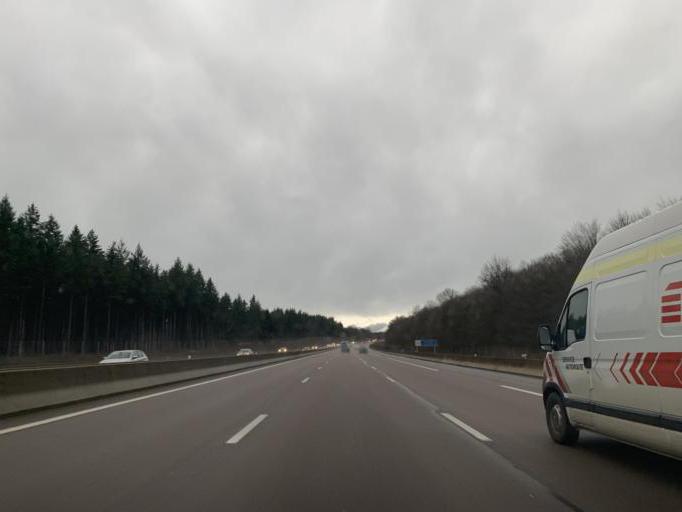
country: FR
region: Bourgogne
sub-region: Departement de la Cote-d'Or
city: Selongey
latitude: 47.6575
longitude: 5.1757
